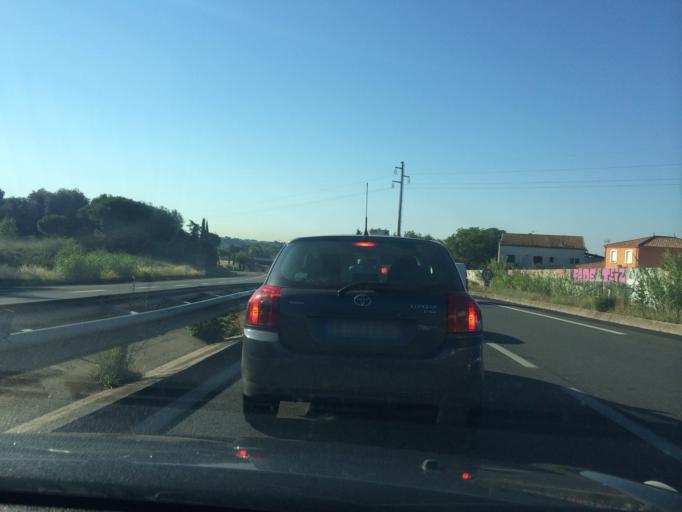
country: FR
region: Languedoc-Roussillon
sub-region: Departement de l'Herault
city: Juvignac
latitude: 43.6125
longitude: 3.8006
